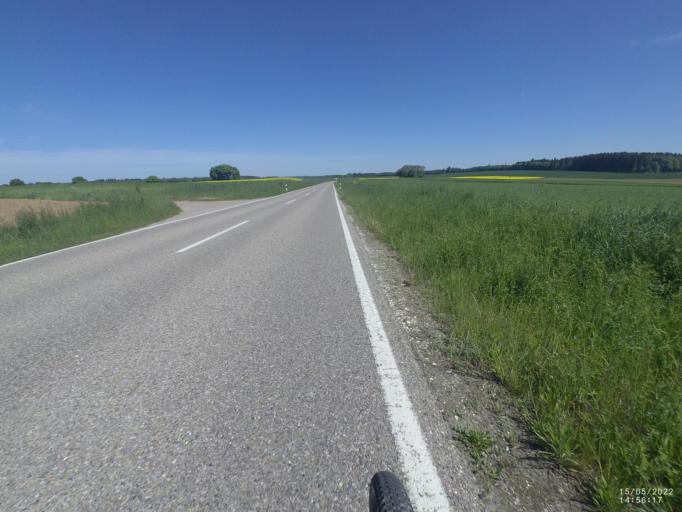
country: DE
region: Baden-Wuerttemberg
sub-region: Regierungsbezirk Stuttgart
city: Bolheim
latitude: 48.6001
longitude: 10.1407
